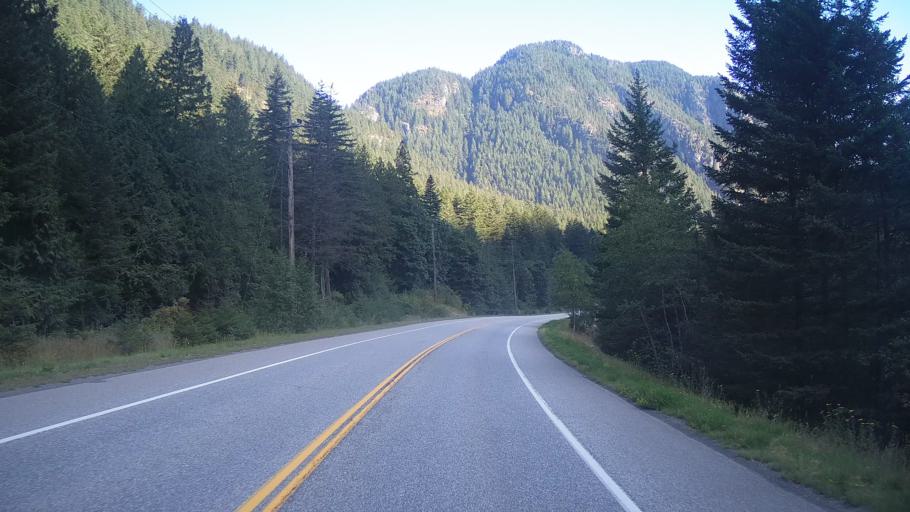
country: CA
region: British Columbia
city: Hope
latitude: 49.6009
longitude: -121.4158
